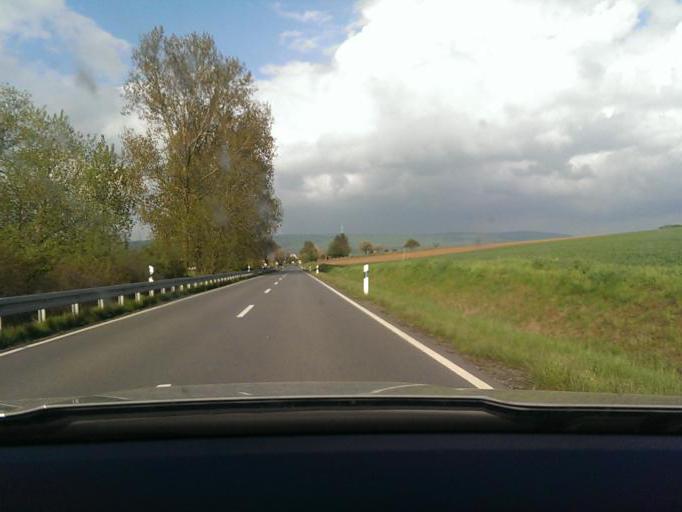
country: DE
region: Lower Saxony
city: Pohle
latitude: 52.2573
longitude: 9.3275
